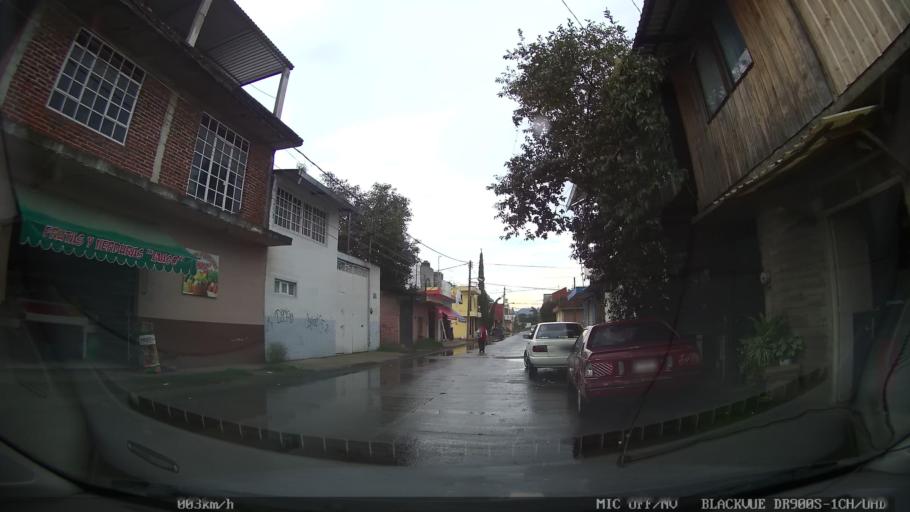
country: MX
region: Michoacan
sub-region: Uruapan
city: Santa Rosa (Santa Barbara)
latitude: 19.3997
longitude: -102.0273
